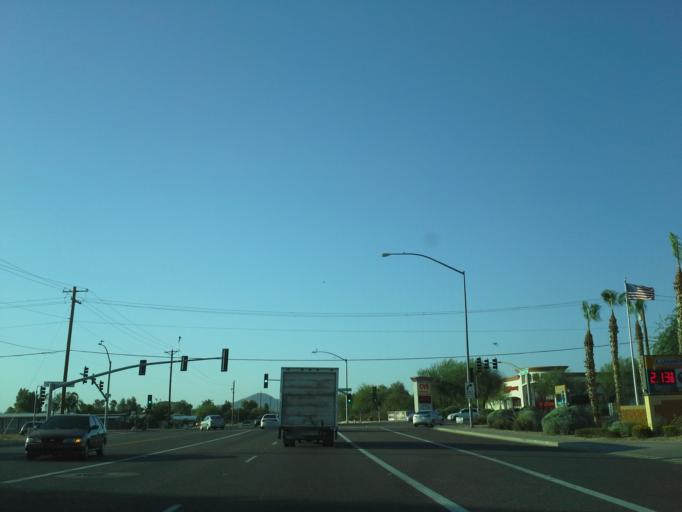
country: US
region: Arizona
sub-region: Pinal County
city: Apache Junction
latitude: 33.4071
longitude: -111.6327
